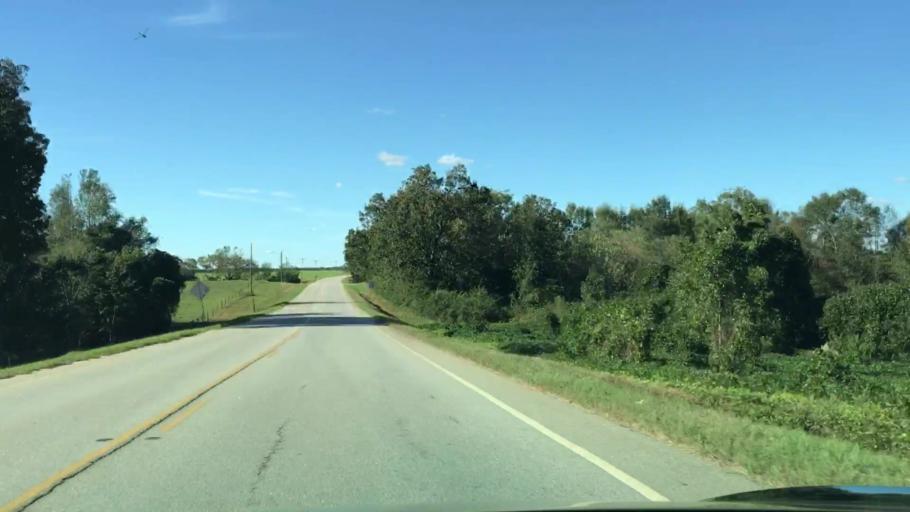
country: US
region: Georgia
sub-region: Jefferson County
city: Louisville
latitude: 33.0718
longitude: -82.4083
